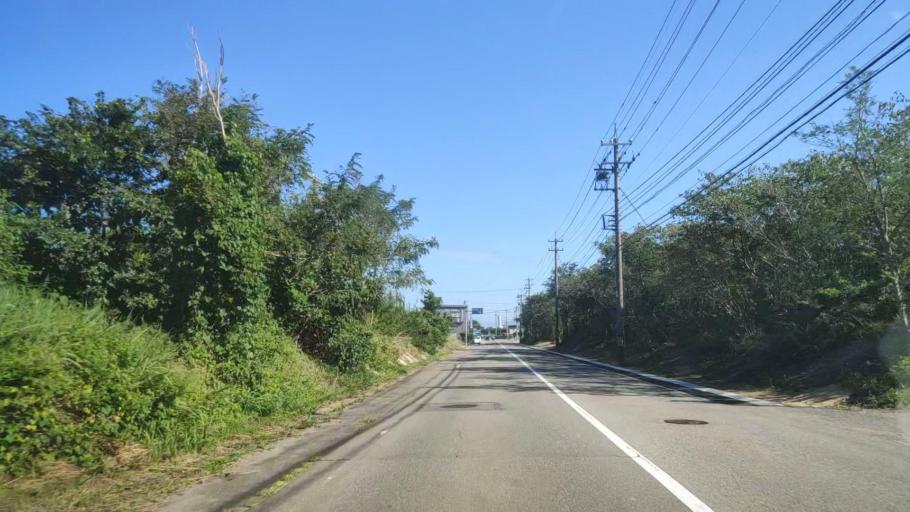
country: JP
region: Ishikawa
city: Hakui
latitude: 36.9761
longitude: 136.7758
